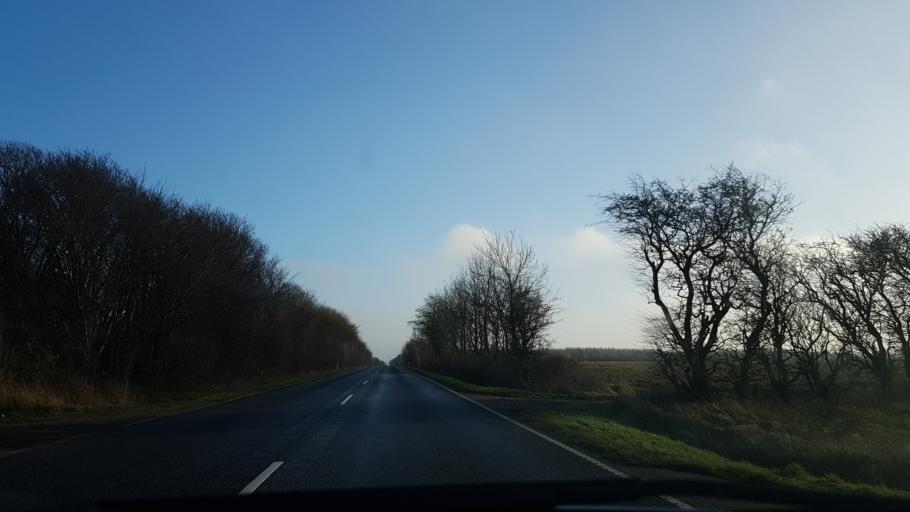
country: DK
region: South Denmark
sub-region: Haderslev Kommune
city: Vojens
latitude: 55.1854
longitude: 9.2248
